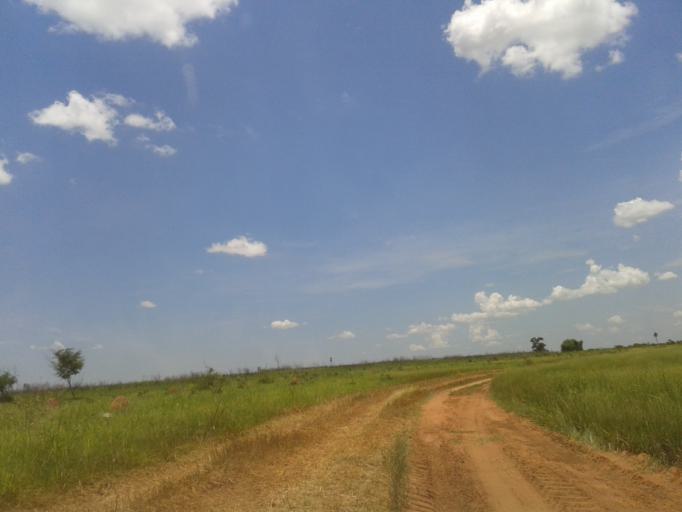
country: BR
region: Minas Gerais
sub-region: Santa Vitoria
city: Santa Vitoria
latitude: -19.2239
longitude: -50.4417
